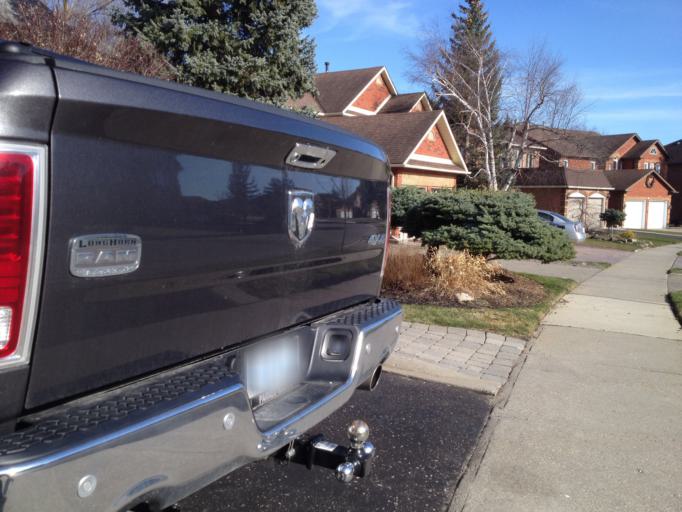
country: CA
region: Ontario
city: Brampton
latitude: 43.7418
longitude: -79.8089
